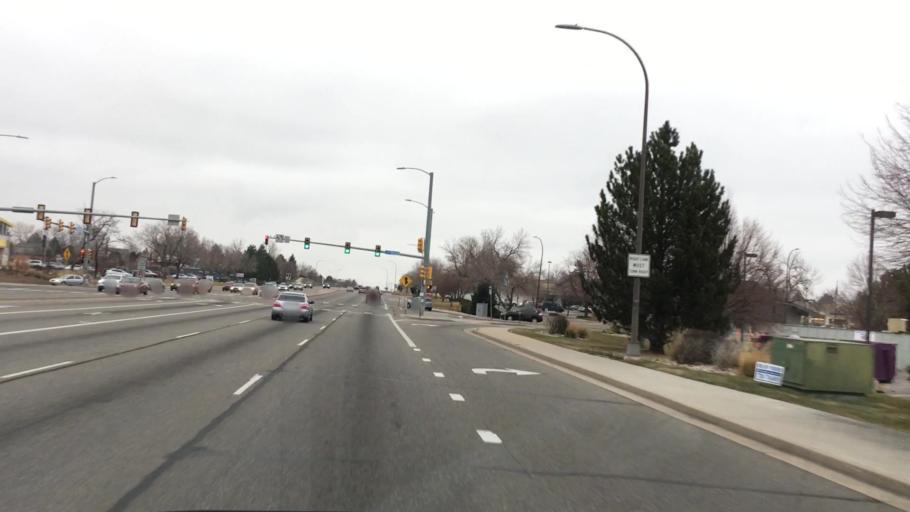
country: US
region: Colorado
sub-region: Jefferson County
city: Arvada
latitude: 39.8411
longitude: -105.0817
